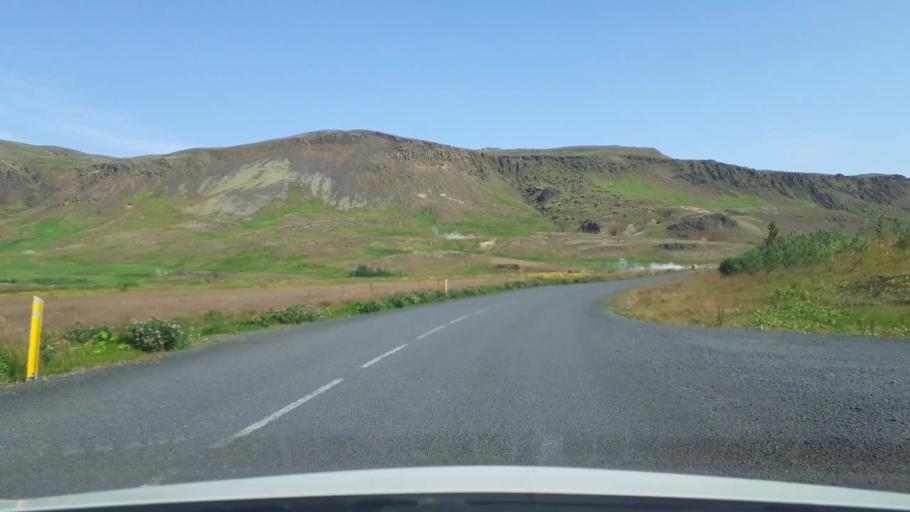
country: IS
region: South
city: Hveragerdi
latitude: 64.0132
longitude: -21.1975
